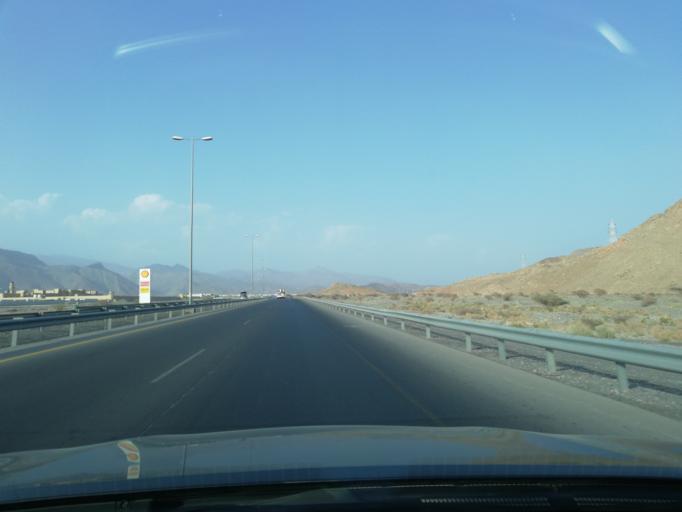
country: OM
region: Muhafazat ad Dakhiliyah
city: Nizwa
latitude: 22.8819
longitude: 57.6252
